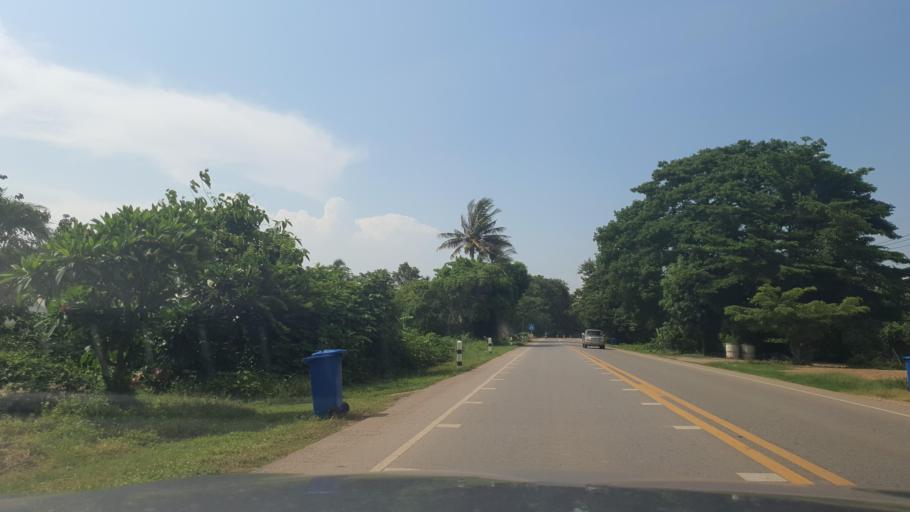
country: TH
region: Sukhothai
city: Si Samrong
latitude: 17.1448
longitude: 99.8238
